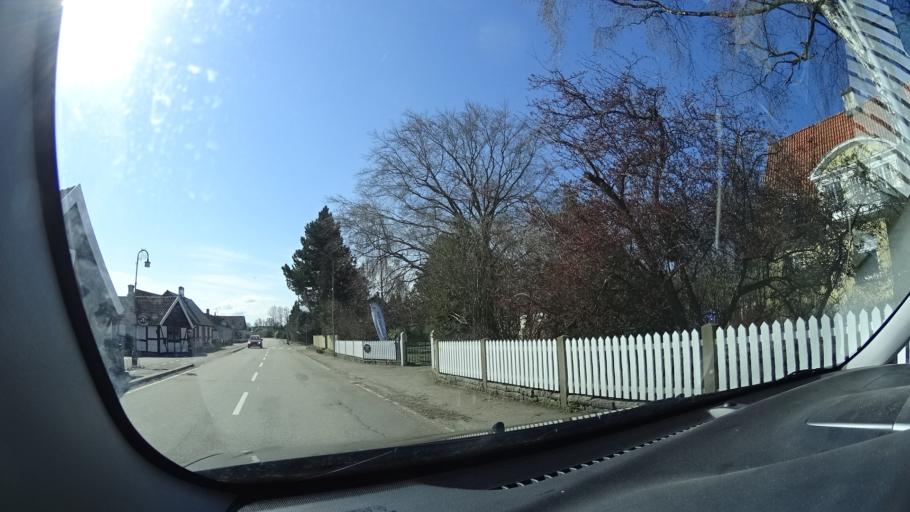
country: SE
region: Skane
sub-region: Hoganas Kommun
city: Hoganas
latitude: 56.2250
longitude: 12.6740
